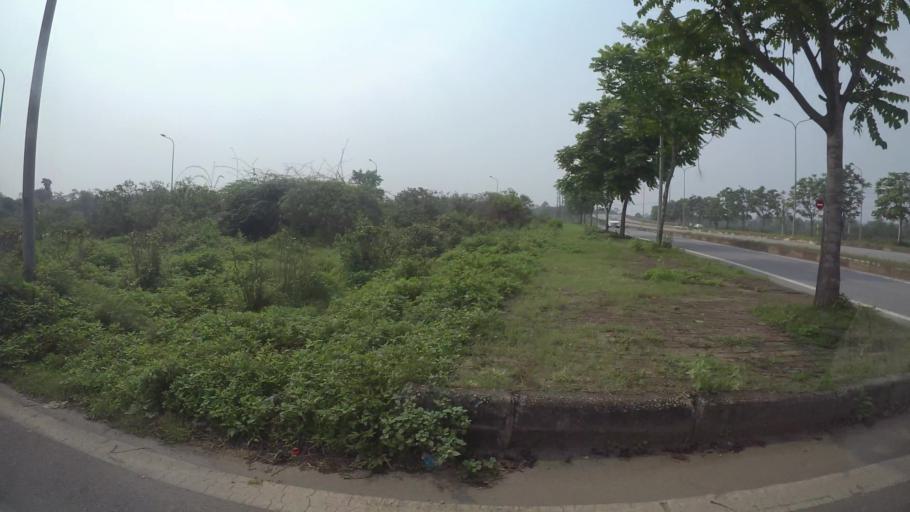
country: VN
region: Ha Noi
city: Lien Quan
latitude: 20.9932
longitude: 105.5358
